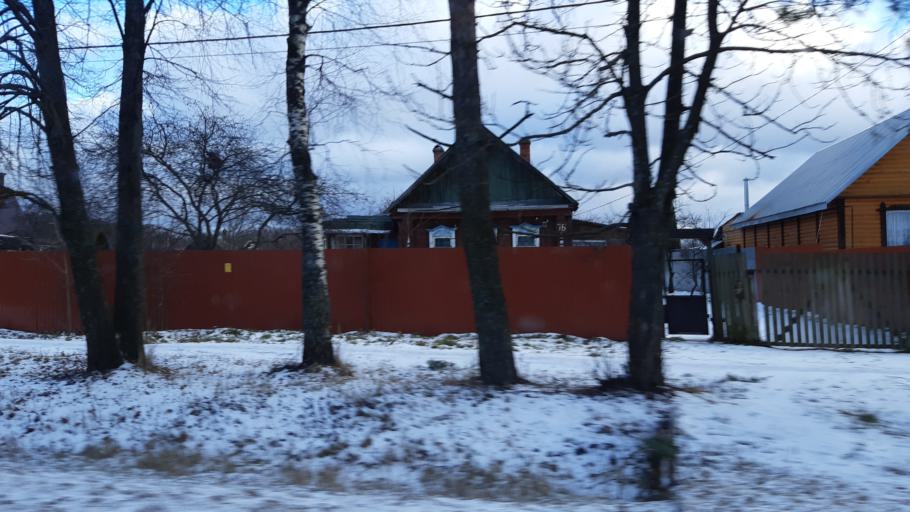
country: RU
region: Moskovskaya
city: Noginsk-9
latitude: 55.9947
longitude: 38.5433
